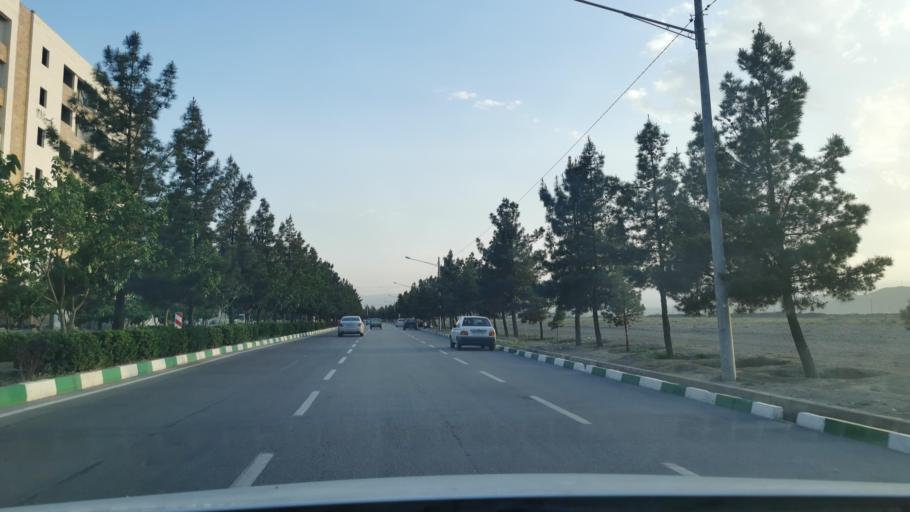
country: IR
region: Razavi Khorasan
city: Torqabeh
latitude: 36.3897
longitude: 59.4686
